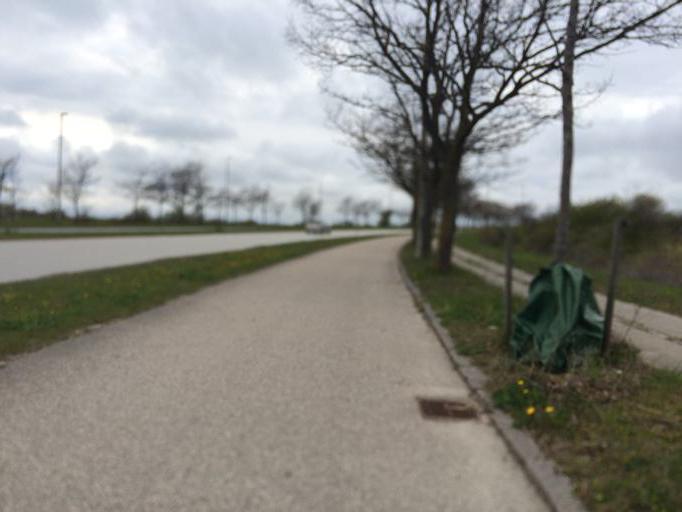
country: DK
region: Capital Region
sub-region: Hvidovre Kommune
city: Hvidovre
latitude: 55.6140
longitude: 12.4472
